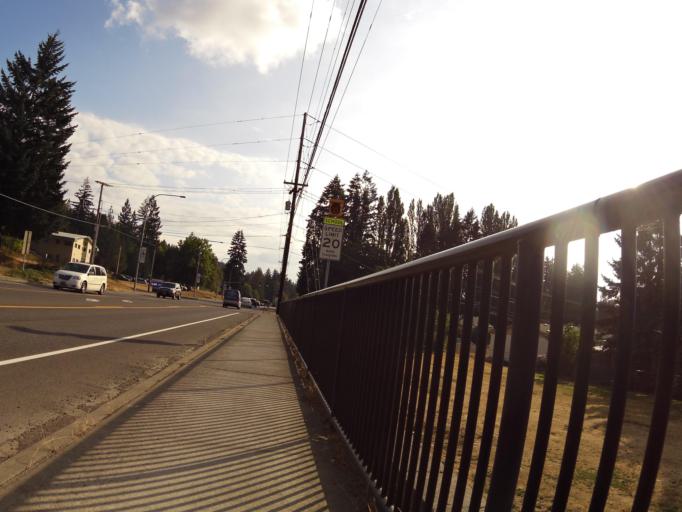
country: US
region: Washington
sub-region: Mason County
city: Belfair
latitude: 47.4404
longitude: -122.8343
